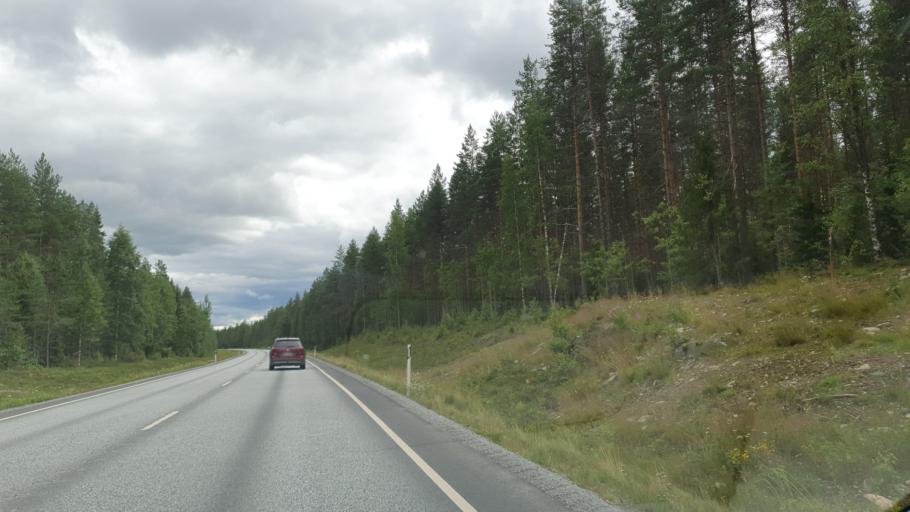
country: FI
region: Northern Savo
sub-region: Ylae-Savo
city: Sonkajaervi
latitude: 63.9094
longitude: 27.3863
